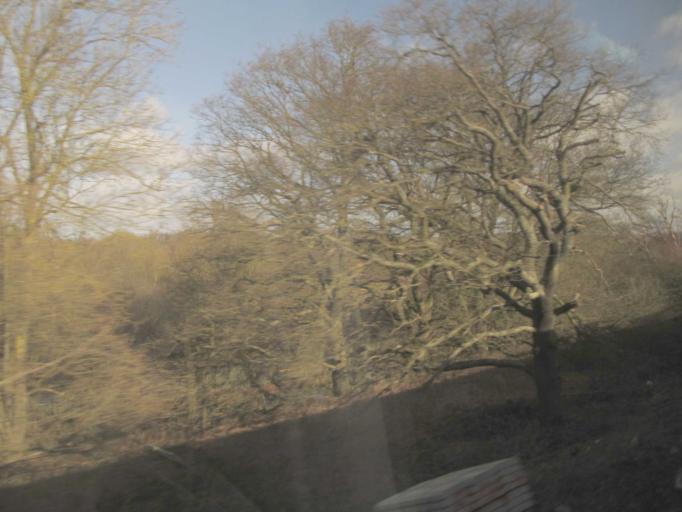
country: GB
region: England
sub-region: Wokingham
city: Charvil
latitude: 51.4696
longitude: -0.8774
